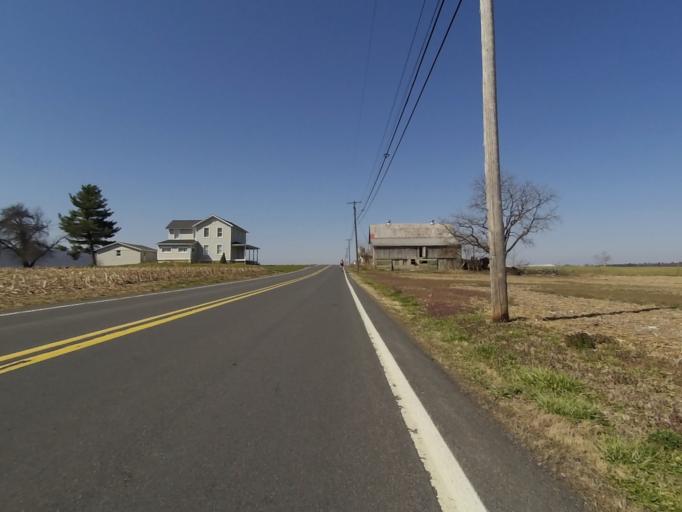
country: US
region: Pennsylvania
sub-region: Centre County
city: Pine Grove Mills
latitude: 40.7261
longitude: -77.9413
